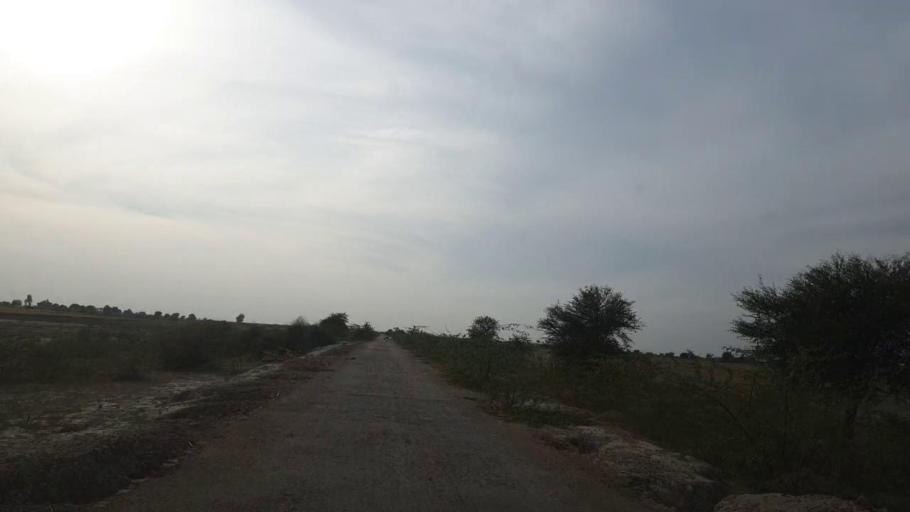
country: PK
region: Sindh
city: Nabisar
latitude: 24.9974
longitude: 69.5254
